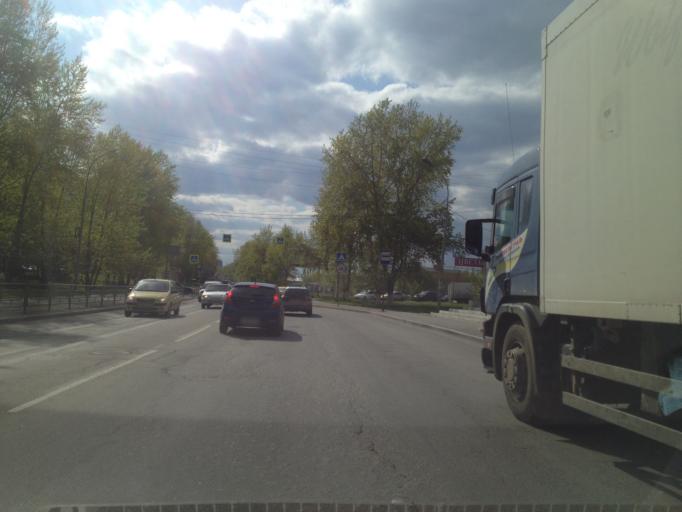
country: RU
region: Sverdlovsk
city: Yekaterinburg
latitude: 56.8576
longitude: 60.5668
